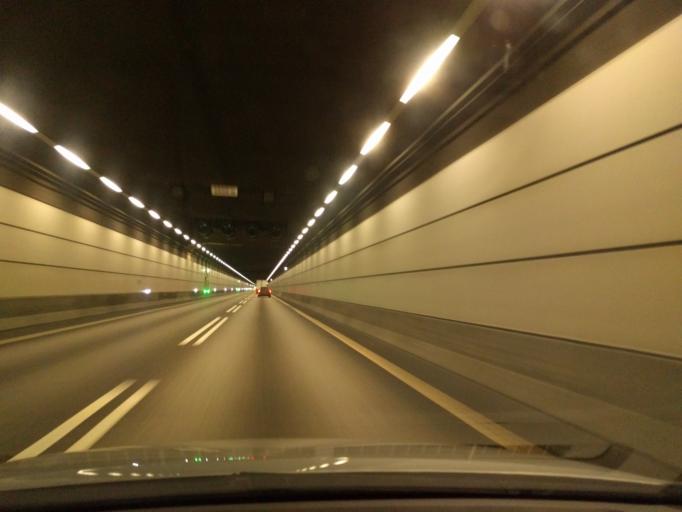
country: DK
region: Capital Region
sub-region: Dragor Kommune
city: Dragor
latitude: 55.6130
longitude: 12.7222
